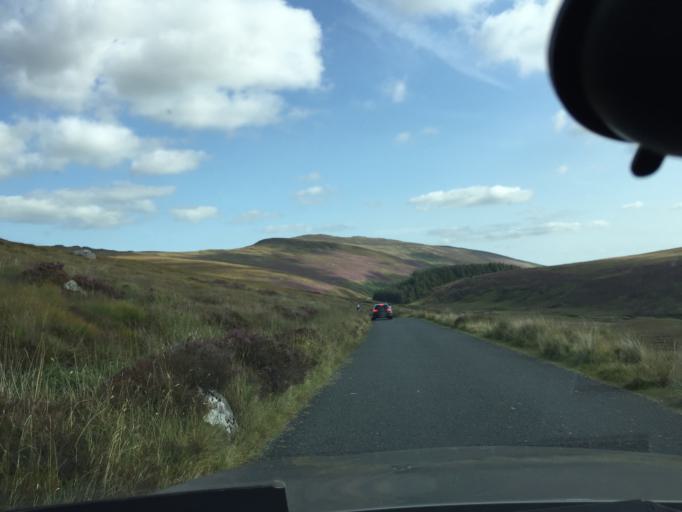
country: IE
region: Leinster
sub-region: Wicklow
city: Rathdrum
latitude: 53.0719
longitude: -6.3503
